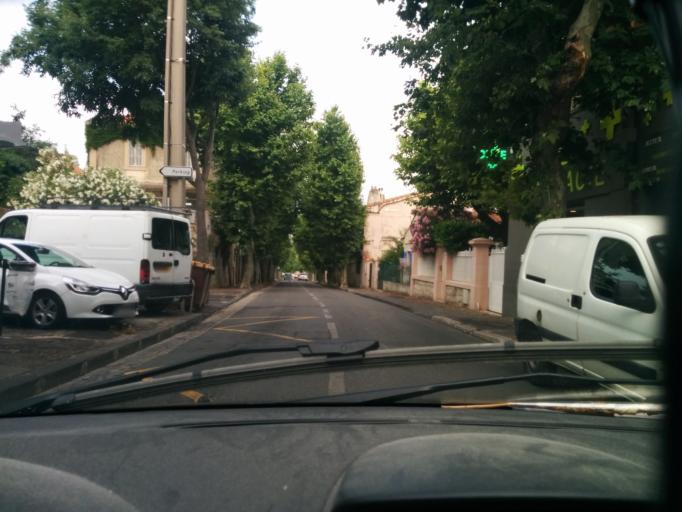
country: FR
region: Provence-Alpes-Cote d'Azur
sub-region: Departement des Bouches-du-Rhone
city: Plan-de-Cuques
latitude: 43.3252
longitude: 5.4546
